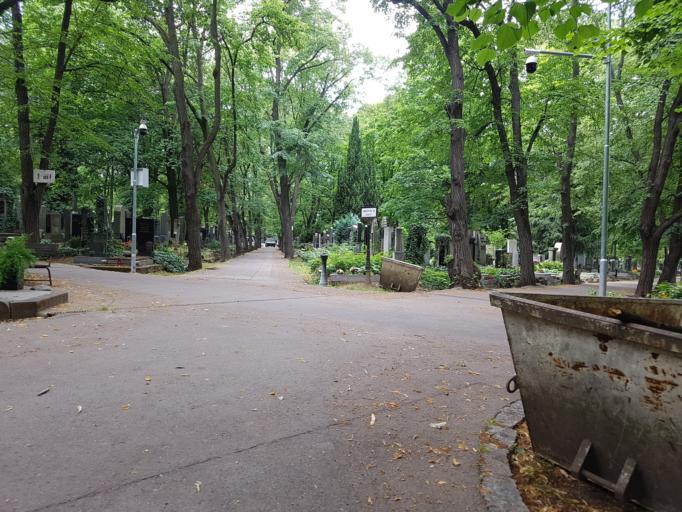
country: CZ
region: Praha
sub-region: Praha 8
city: Karlin
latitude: 50.0796
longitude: 14.4689
